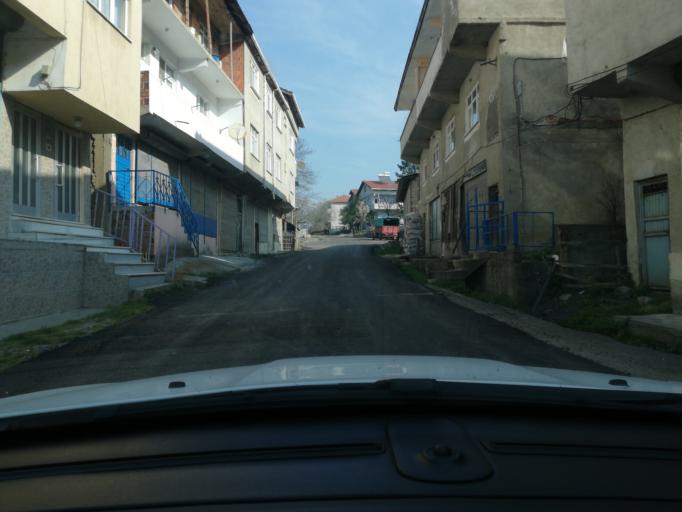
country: TR
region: Karabuk
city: Yenice
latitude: 41.2625
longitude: 32.3639
